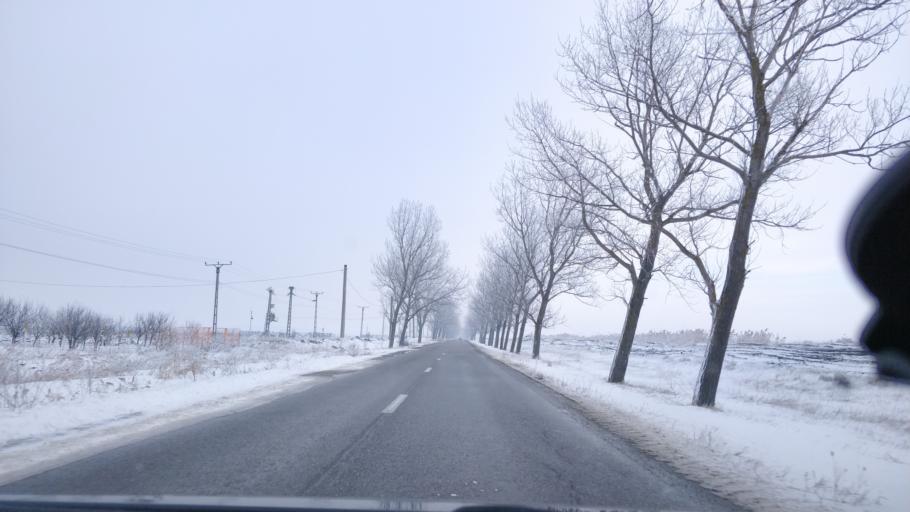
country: RO
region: Vrancea
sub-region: Comuna Vanatori
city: Jorasti
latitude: 45.6975
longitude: 27.2489
